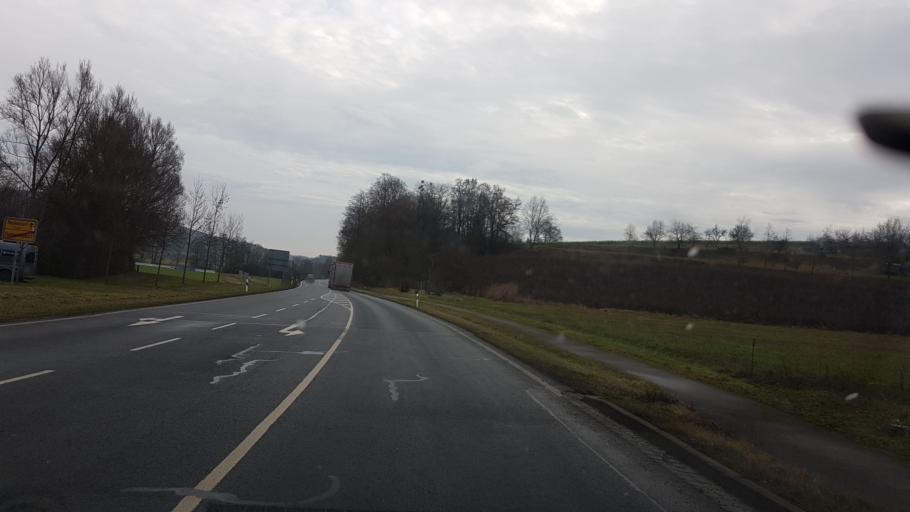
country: DE
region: Bavaria
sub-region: Regierungsbezirk Unterfranken
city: Rentweinsdorf
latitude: 50.0597
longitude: 10.8043
